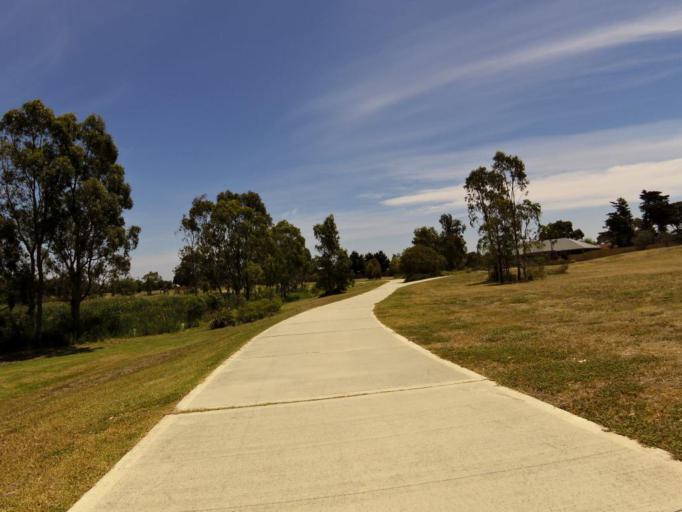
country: AU
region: Victoria
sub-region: Hobsons Bay
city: Laverton
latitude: -37.8739
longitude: 144.7644
